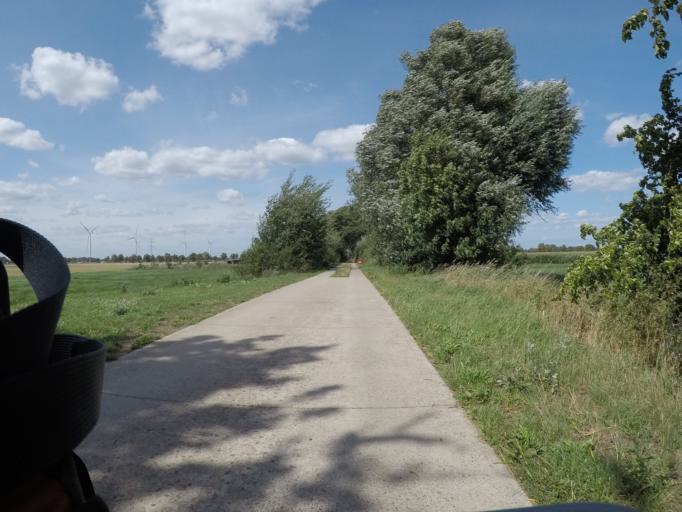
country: DE
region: Lower Saxony
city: Stelle
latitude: 53.4562
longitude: 10.1158
